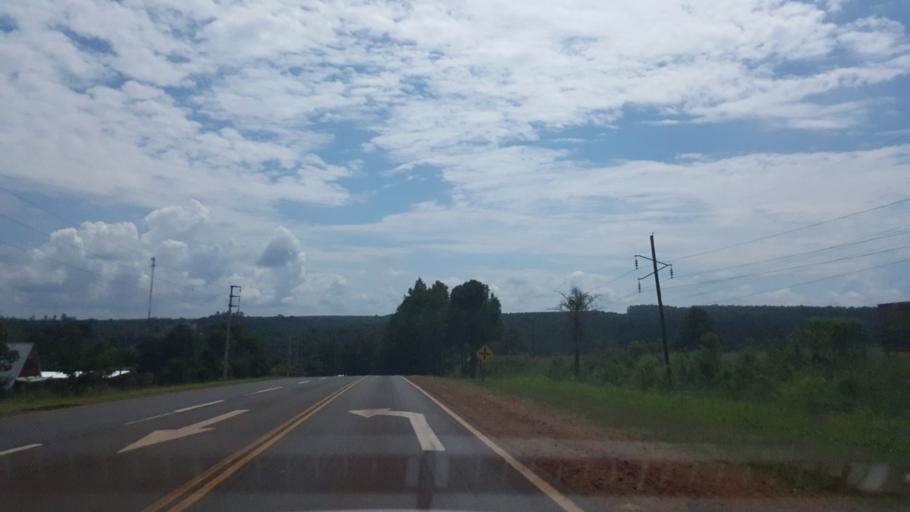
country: AR
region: Misiones
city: Capiovi
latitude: -26.8673
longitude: -55.0459
